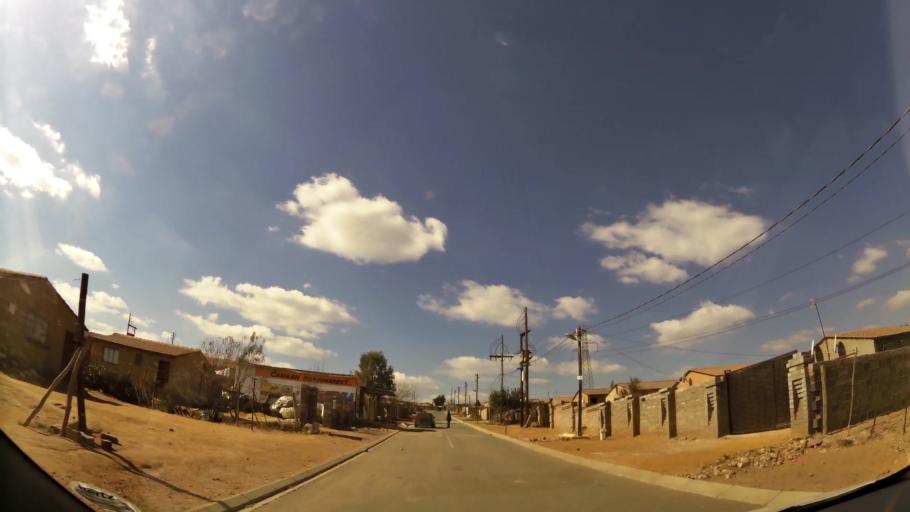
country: ZA
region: Gauteng
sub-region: West Rand District Municipality
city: Krugersdorp
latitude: -26.1379
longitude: 27.7845
